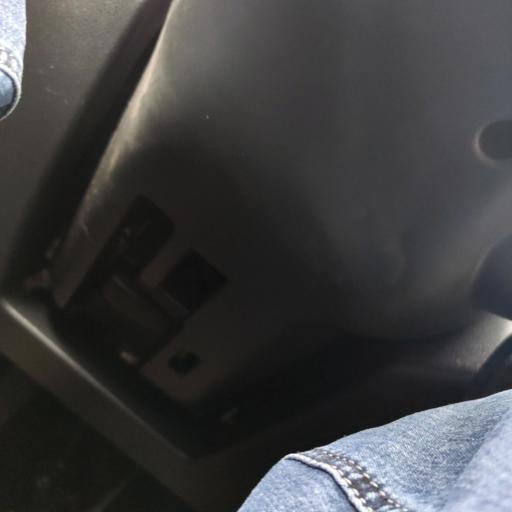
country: RU
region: Samara
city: Smyshlyayevka
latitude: 53.2141
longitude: 50.3284
